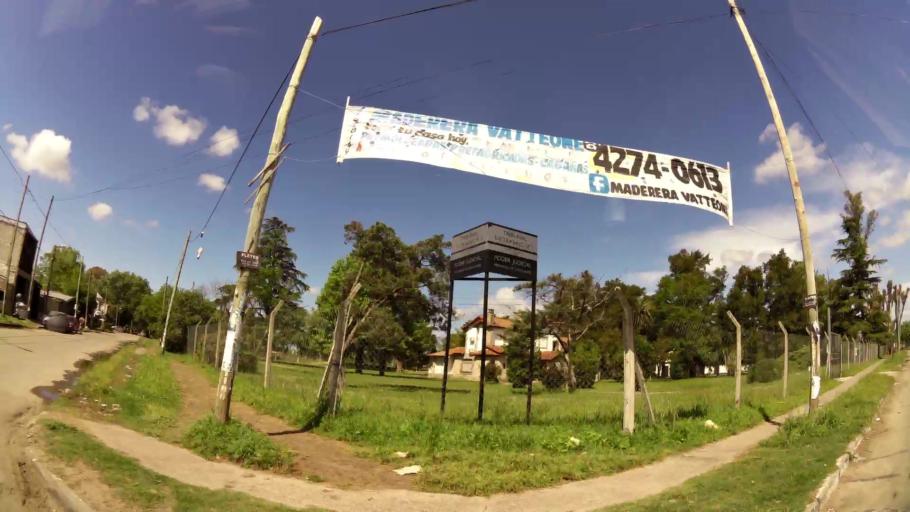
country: AR
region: Buenos Aires
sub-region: Partido de Quilmes
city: Quilmes
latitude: -34.8199
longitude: -58.2639
